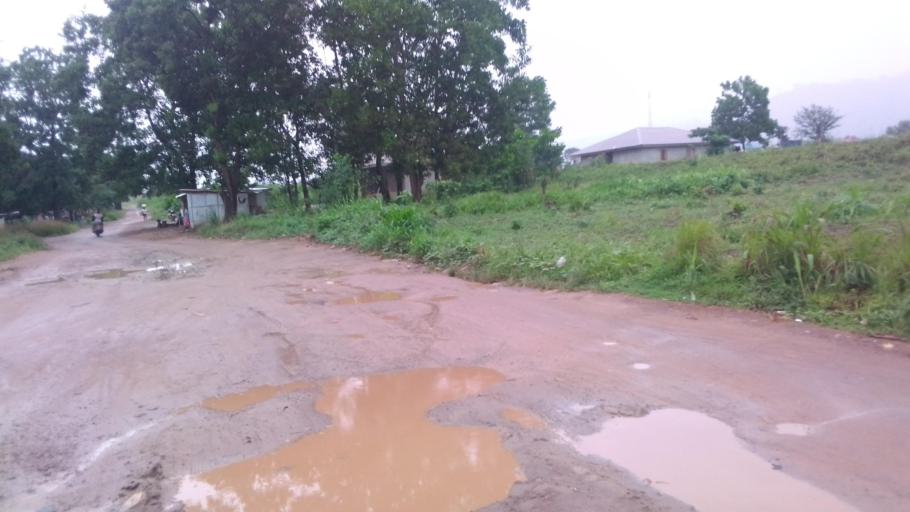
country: SL
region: Eastern Province
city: Kenema
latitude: 7.8992
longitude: -11.1705
